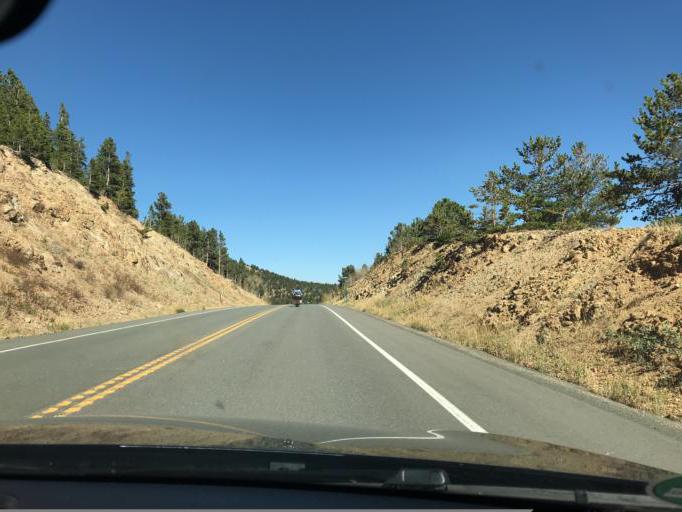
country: US
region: Colorado
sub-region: Boulder County
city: Nederland
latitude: 40.0612
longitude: -105.5199
